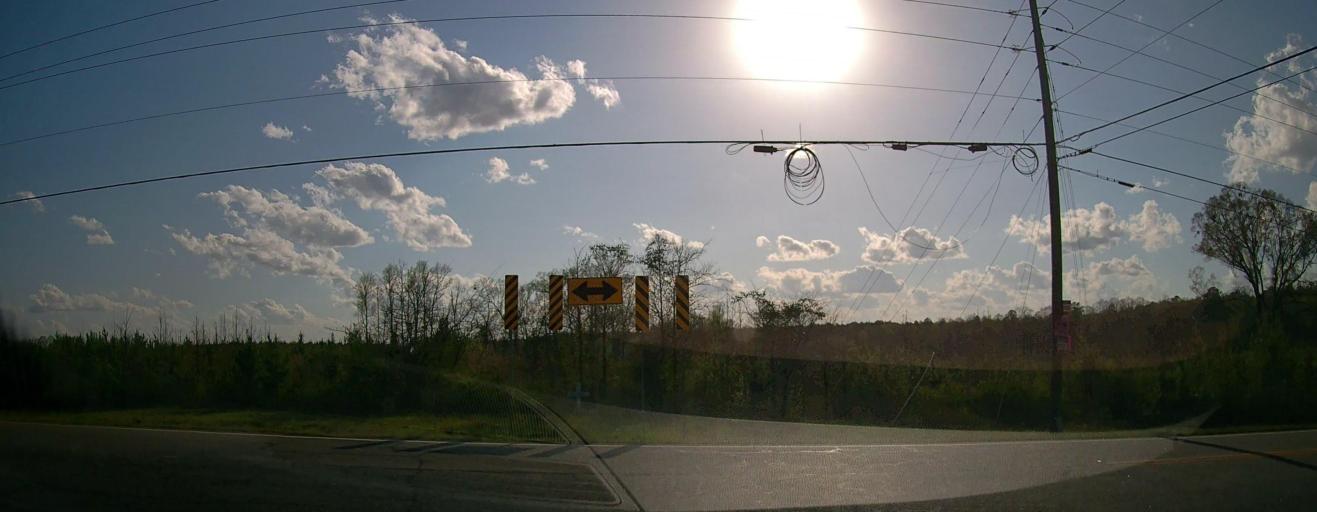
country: US
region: Georgia
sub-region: Putnam County
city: Eatonton
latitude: 33.1962
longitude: -83.4203
